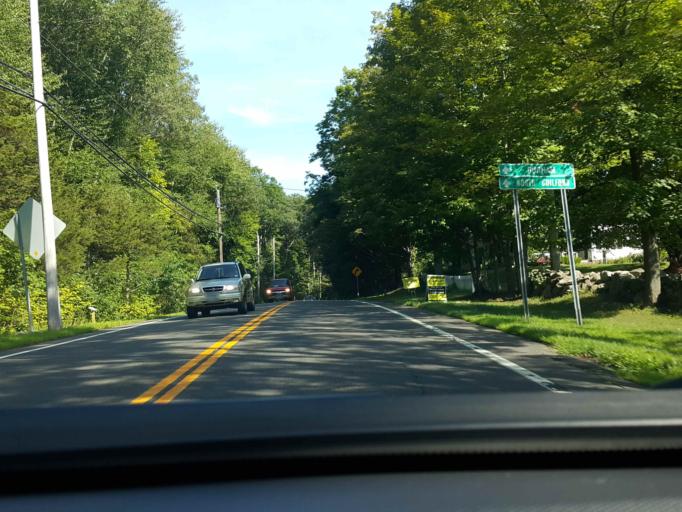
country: US
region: Connecticut
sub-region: New Haven County
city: North Branford
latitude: 41.3540
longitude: -72.7197
